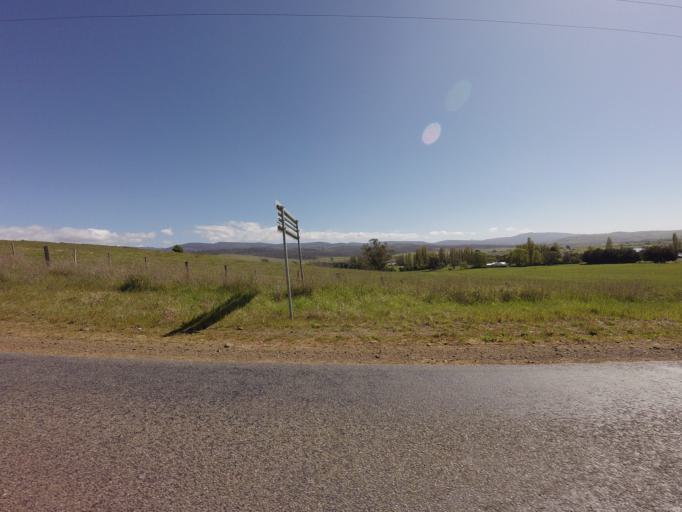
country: AU
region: Tasmania
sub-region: Derwent Valley
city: New Norfolk
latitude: -42.5365
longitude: 146.7531
